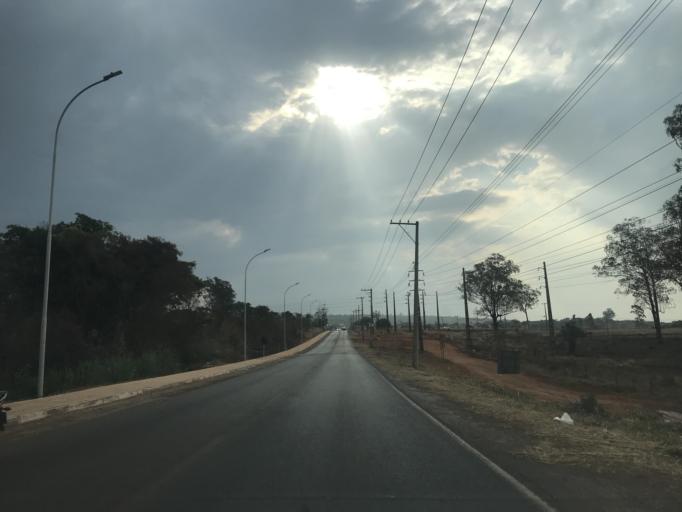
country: BR
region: Federal District
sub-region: Brasilia
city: Brasilia
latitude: -15.6635
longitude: -47.8265
